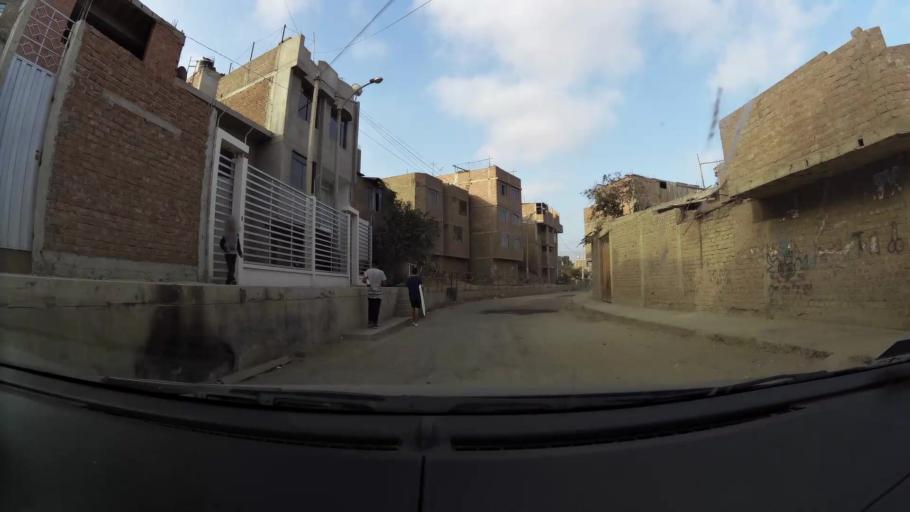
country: PE
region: La Libertad
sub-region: Provincia de Trujillo
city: El Porvenir
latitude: -8.0861
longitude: -79.0165
